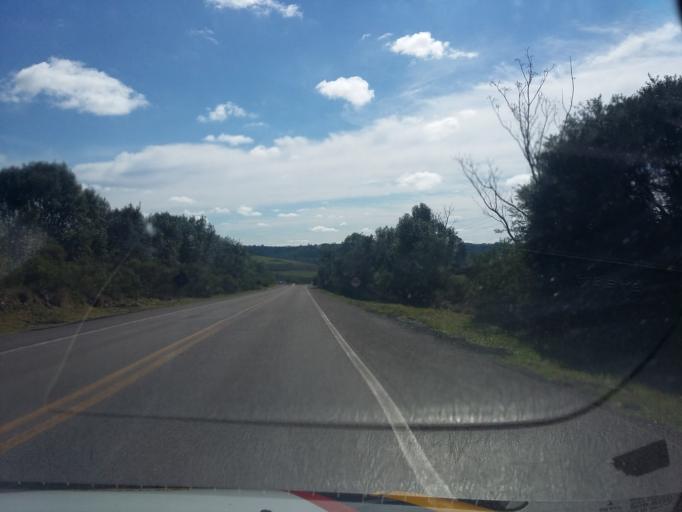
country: BR
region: Rio Grande do Sul
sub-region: Vacaria
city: Vacaria
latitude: -28.6247
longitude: -51.0389
